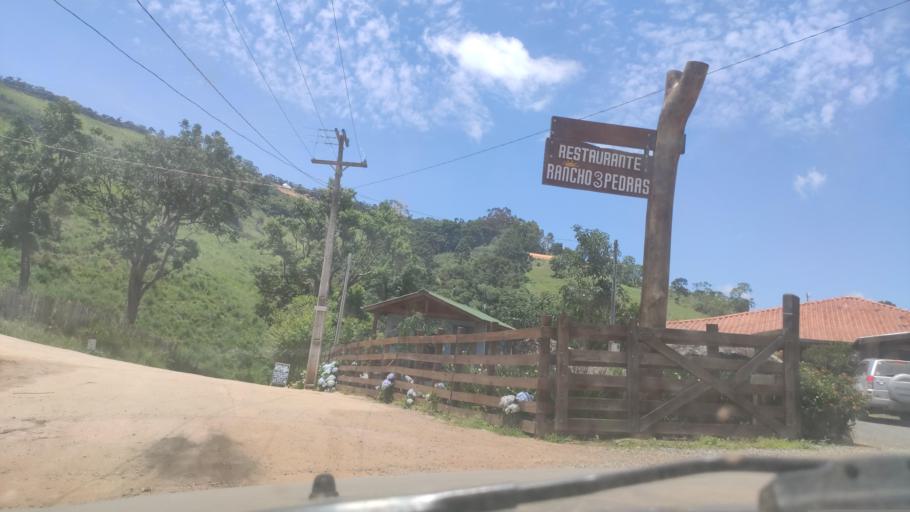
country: BR
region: Minas Gerais
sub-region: Cambui
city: Cambui
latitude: -22.6731
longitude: -45.9645
